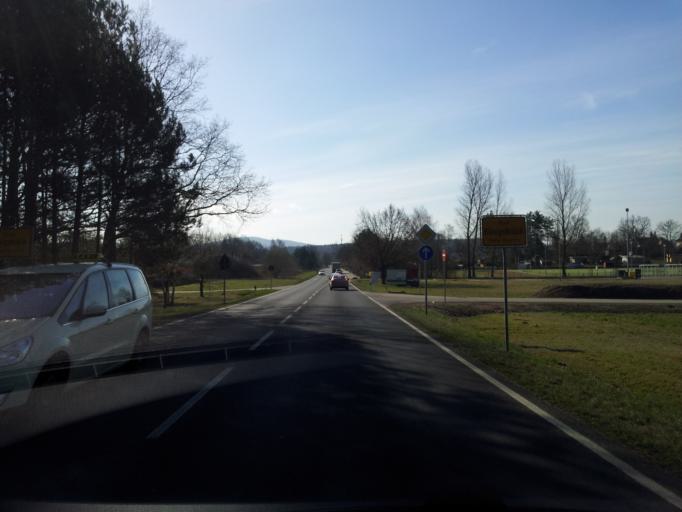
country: DE
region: Saxony
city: Konigsbruck
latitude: 51.2726
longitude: 13.9087
